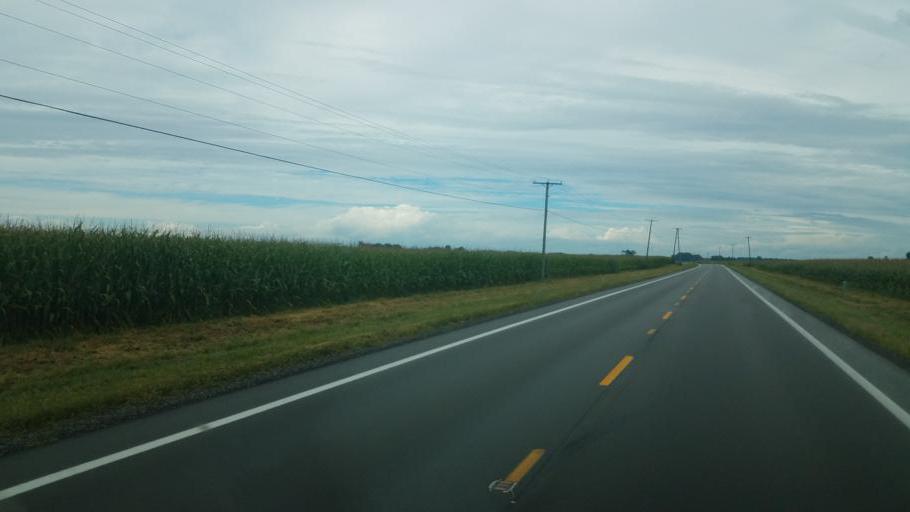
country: US
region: Ohio
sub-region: Delaware County
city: Ashley
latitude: 40.4287
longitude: -82.9527
